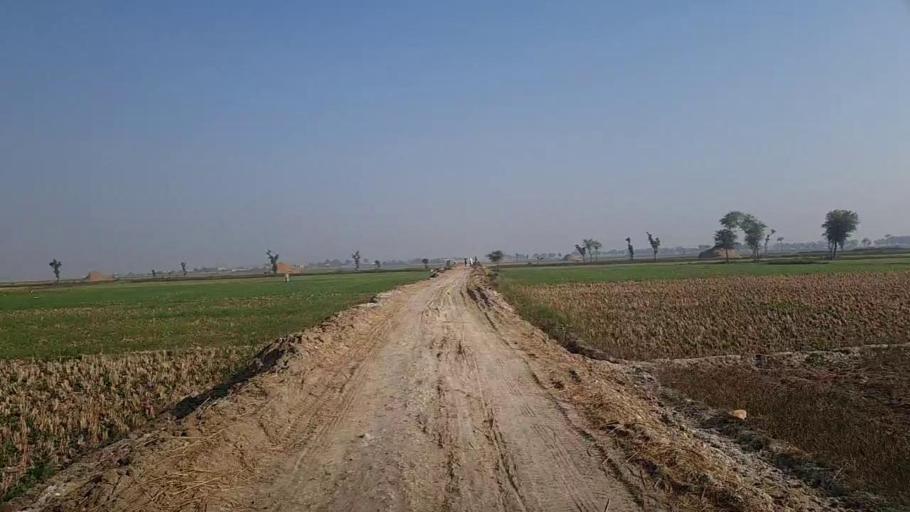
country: PK
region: Sindh
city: Sita Road
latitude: 27.1113
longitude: 67.8924
